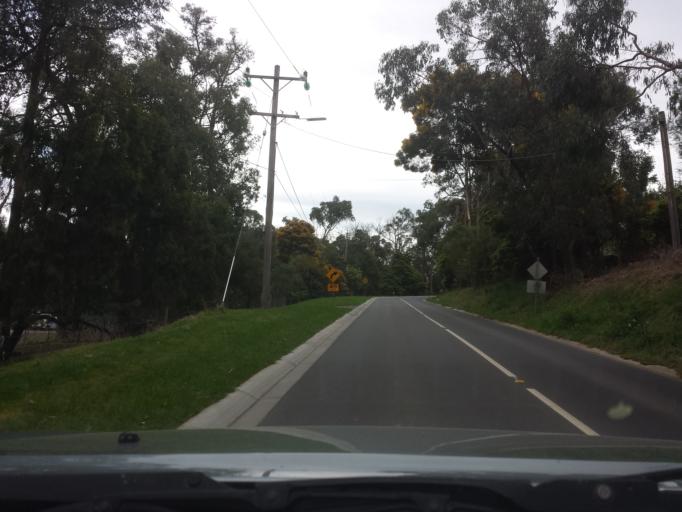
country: AU
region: Victoria
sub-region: Yarra Ranges
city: Mount Evelyn
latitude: -37.7685
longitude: 145.3816
